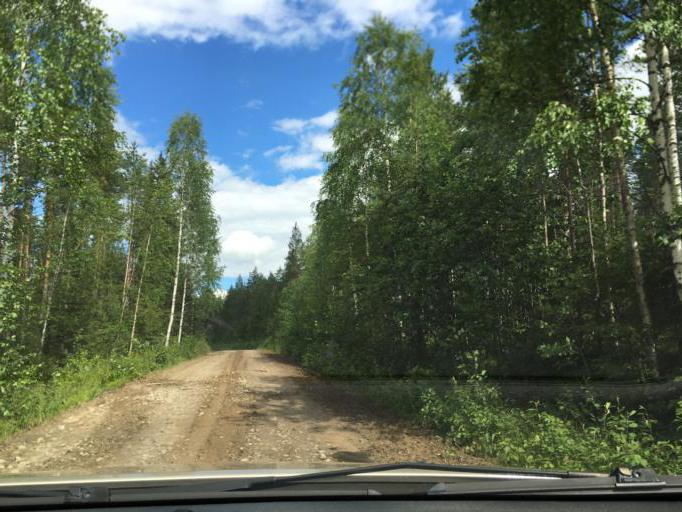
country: SE
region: Norrbotten
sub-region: Overkalix Kommun
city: OEverkalix
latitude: 66.1345
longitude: 22.7839
